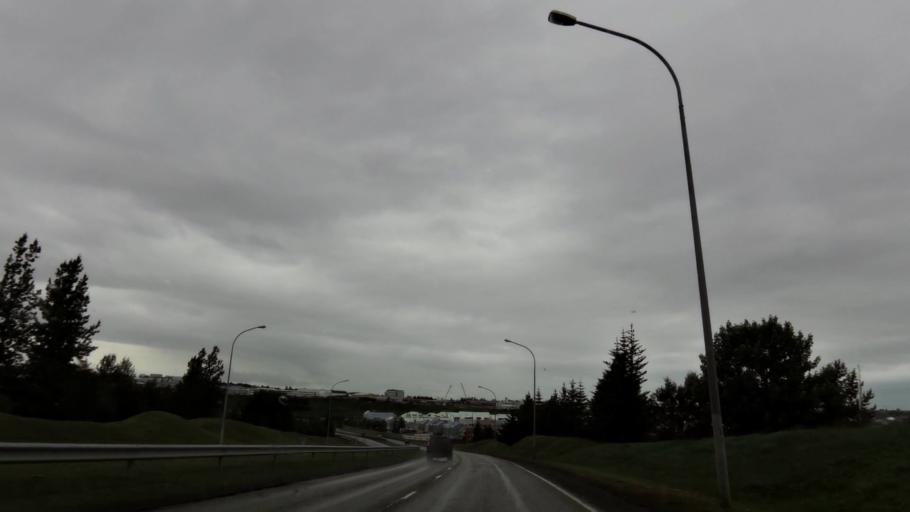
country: IS
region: Capital Region
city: Reykjavik
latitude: 64.1366
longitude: -21.8109
